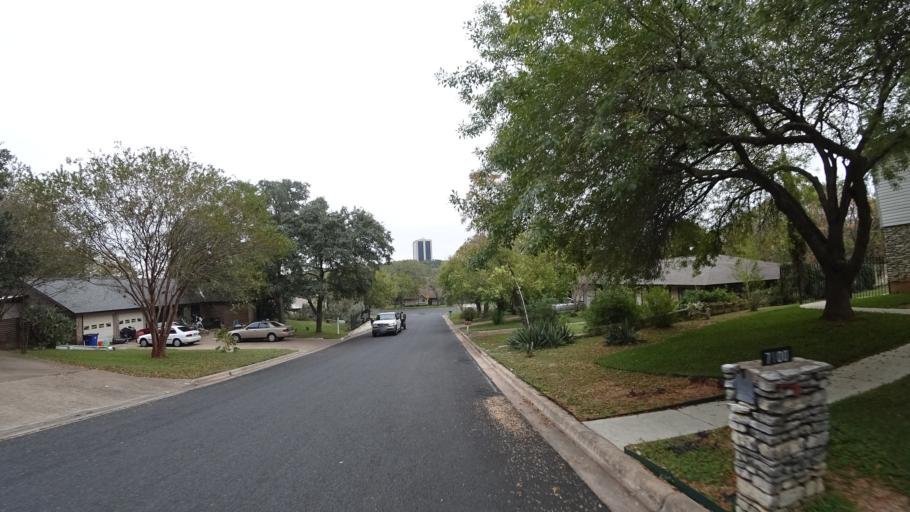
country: US
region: Texas
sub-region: Travis County
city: Barton Creek
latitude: 30.2373
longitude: -97.8841
